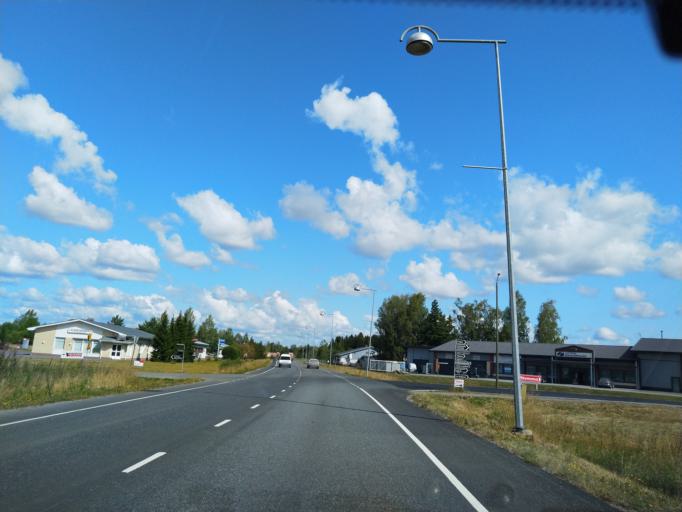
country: FI
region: Satakunta
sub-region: Pori
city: Huittinen
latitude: 61.1685
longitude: 22.7079
